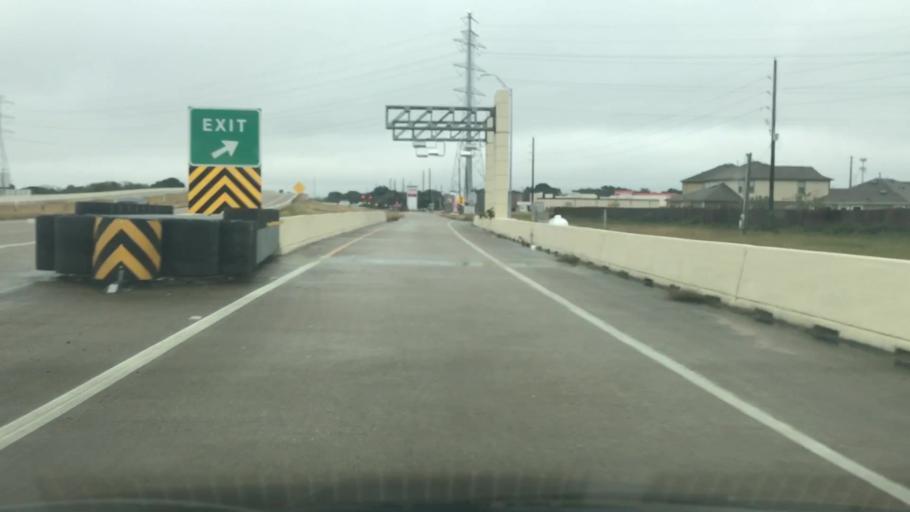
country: US
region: Texas
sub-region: Harris County
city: Katy
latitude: 29.8284
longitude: -95.7628
